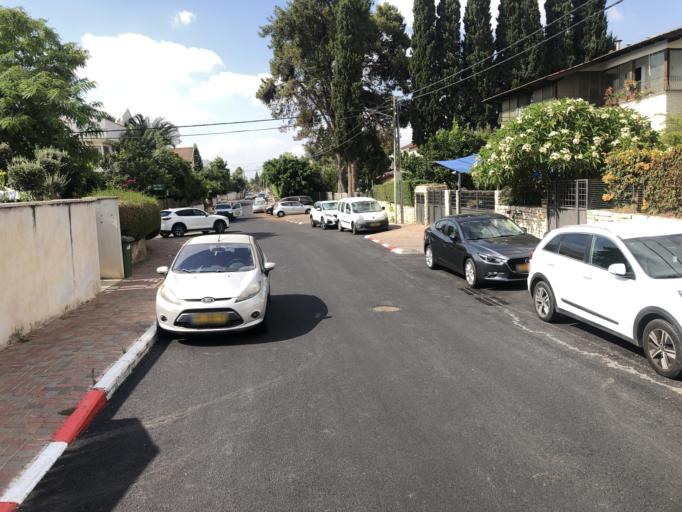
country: IL
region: Central District
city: Yehud
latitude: 32.0396
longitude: 34.8844
